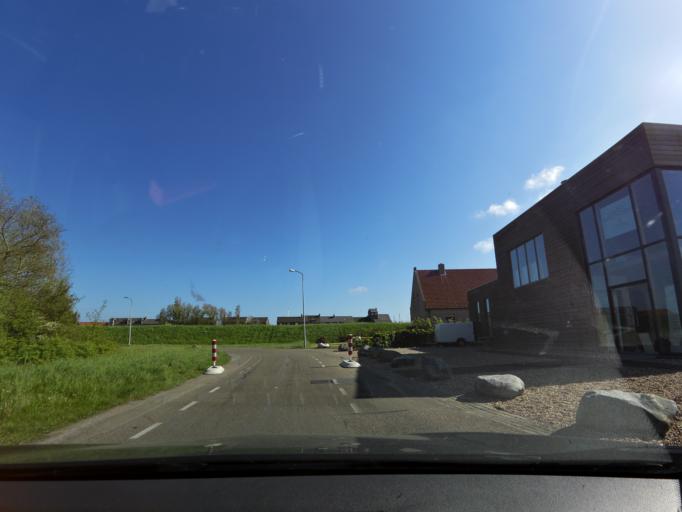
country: NL
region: South Holland
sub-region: Gemeente Goeree-Overflakkee
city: Ouddorp
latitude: 51.7999
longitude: 3.9341
